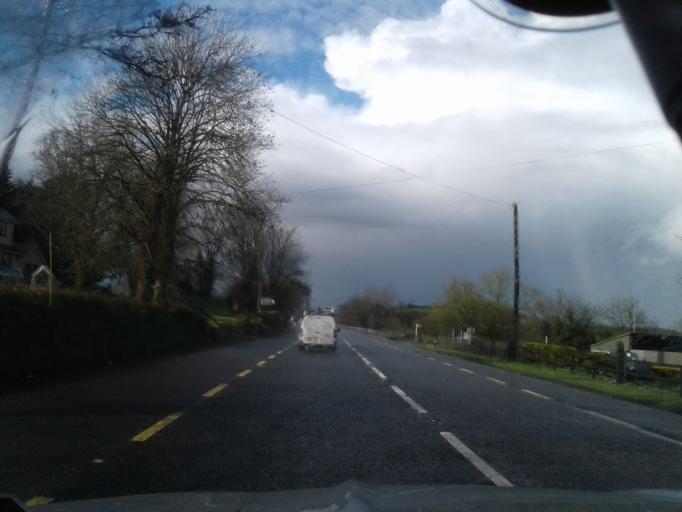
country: IE
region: Ulster
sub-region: County Monaghan
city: Monaghan
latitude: 54.3896
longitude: -6.9731
